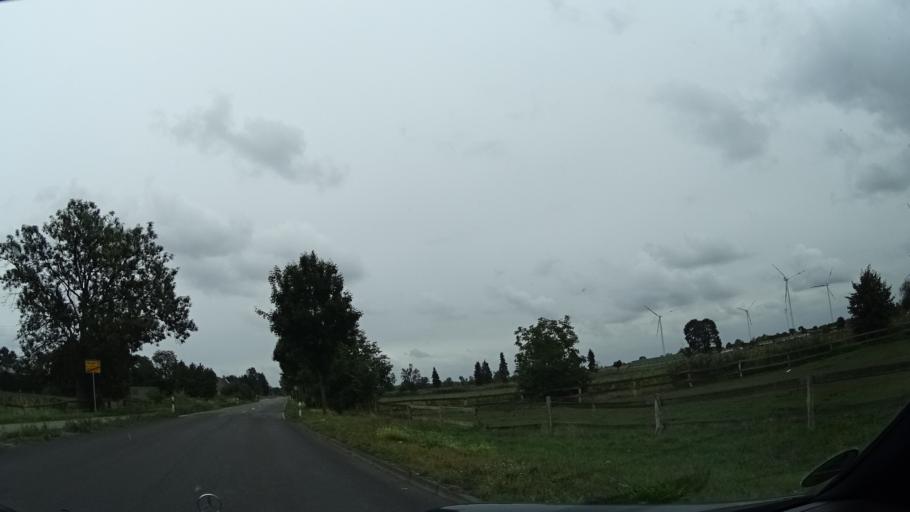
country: DE
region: Brandenburg
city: Dabergotz
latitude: 52.9256
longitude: 12.7478
